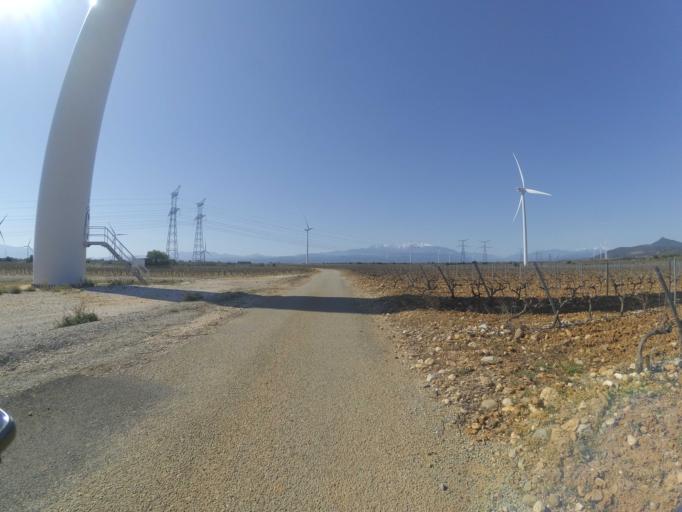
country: FR
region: Languedoc-Roussillon
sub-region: Departement des Pyrenees-Orientales
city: Pezilla-la-Riviere
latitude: 42.7262
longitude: 2.7718
